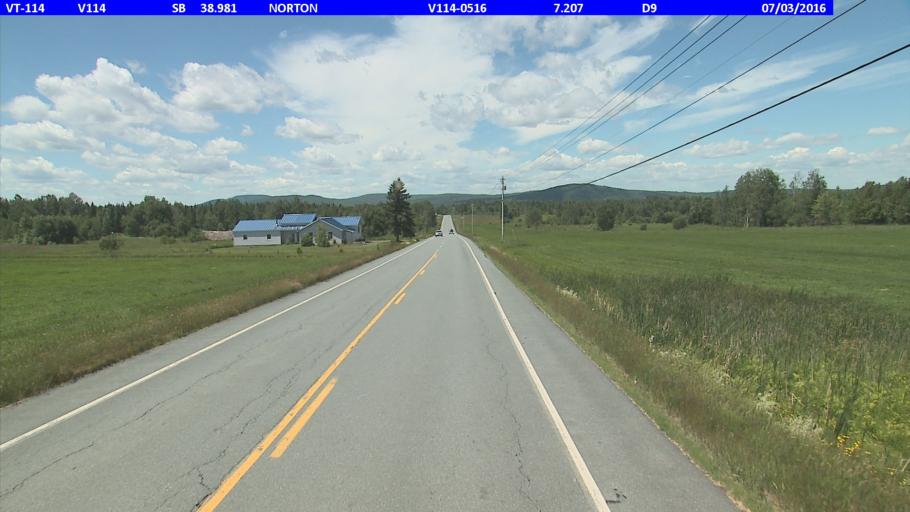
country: CA
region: Quebec
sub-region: Estrie
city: Coaticook
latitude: 45.0026
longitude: -71.7600
